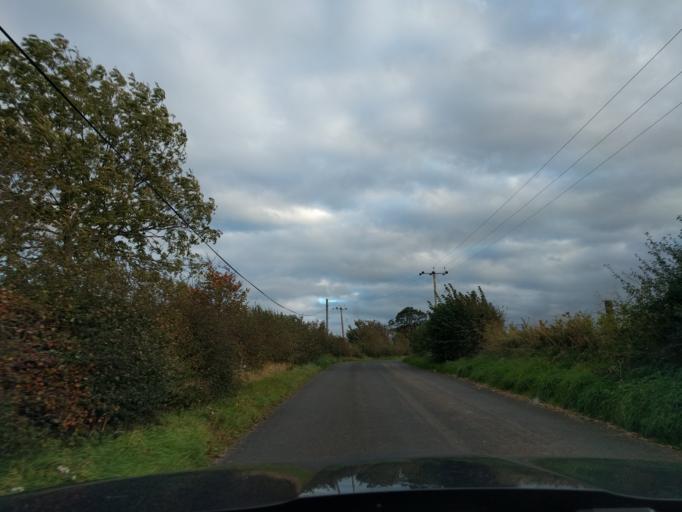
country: GB
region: England
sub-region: Northumberland
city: Ford
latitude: 55.7411
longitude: -2.1097
